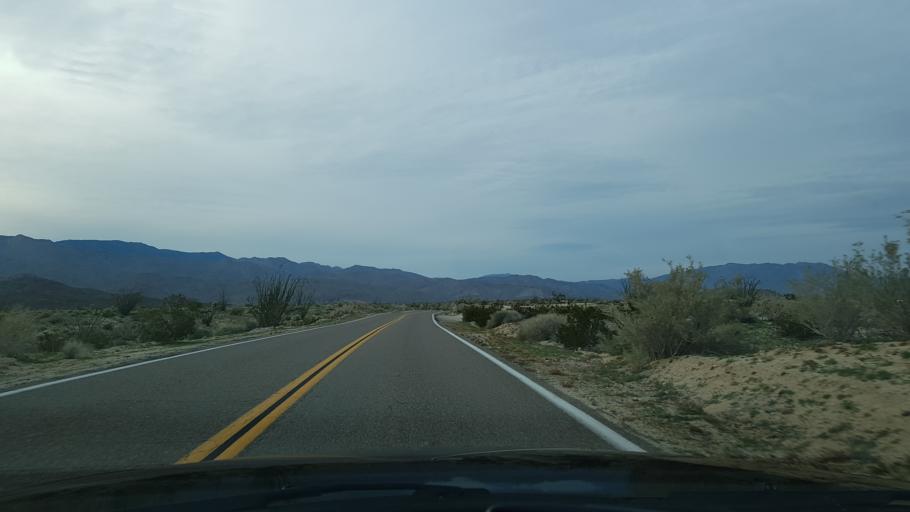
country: MX
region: Baja California
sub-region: Tecate
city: Cereso del Hongo
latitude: 32.8236
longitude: -116.1608
